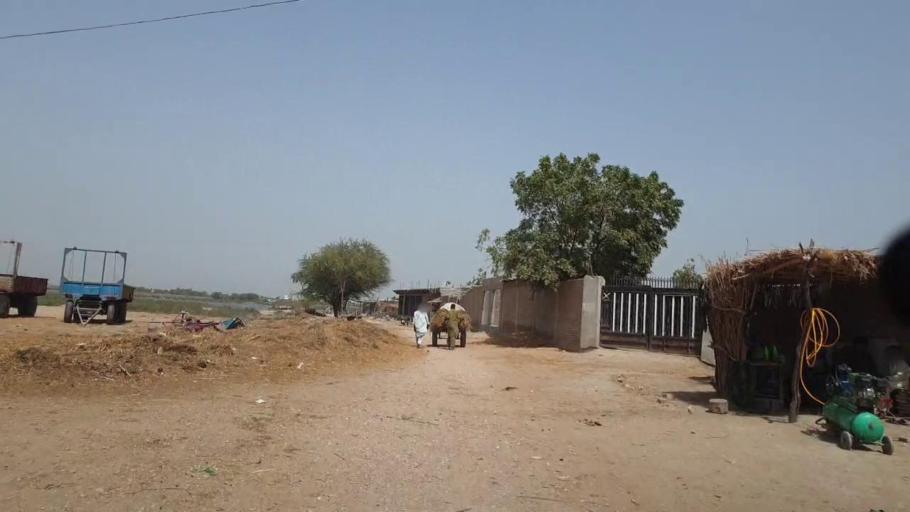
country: PK
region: Sindh
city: Matli
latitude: 25.0625
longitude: 68.7072
